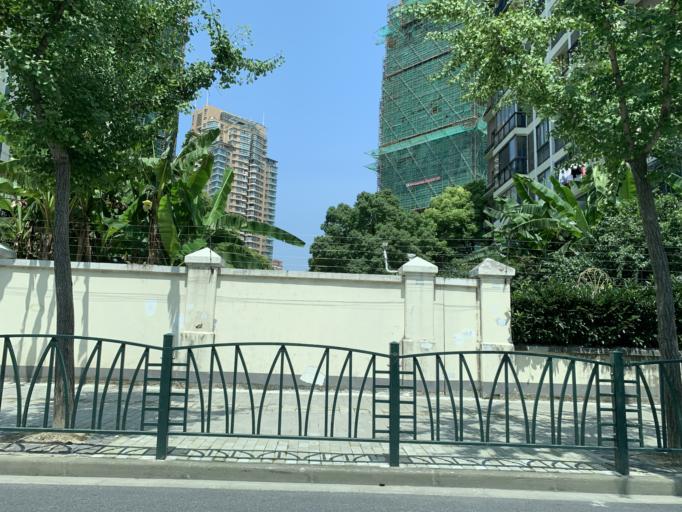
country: CN
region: Shanghai Shi
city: Huamu
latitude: 31.2070
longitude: 121.5149
